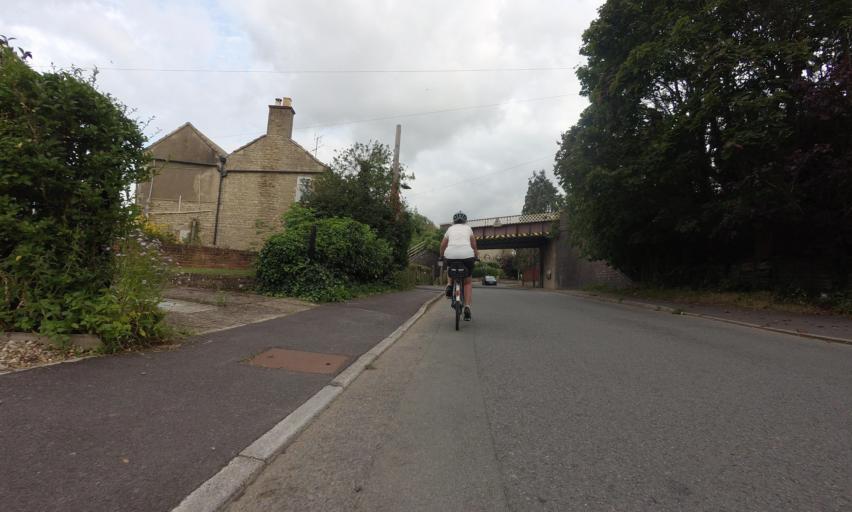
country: GB
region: England
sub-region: Gloucestershire
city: Winchcombe
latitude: 51.9729
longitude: -1.9922
